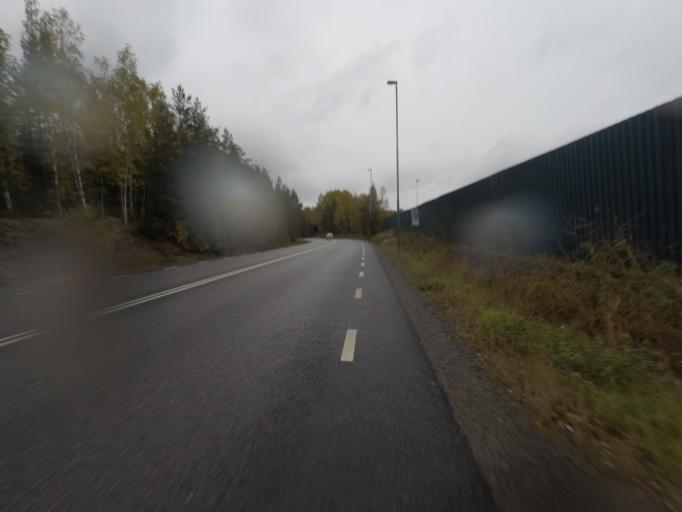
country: SE
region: OErebro
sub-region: Karlskoga Kommun
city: Karlskoga
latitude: 59.3188
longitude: 14.4731
